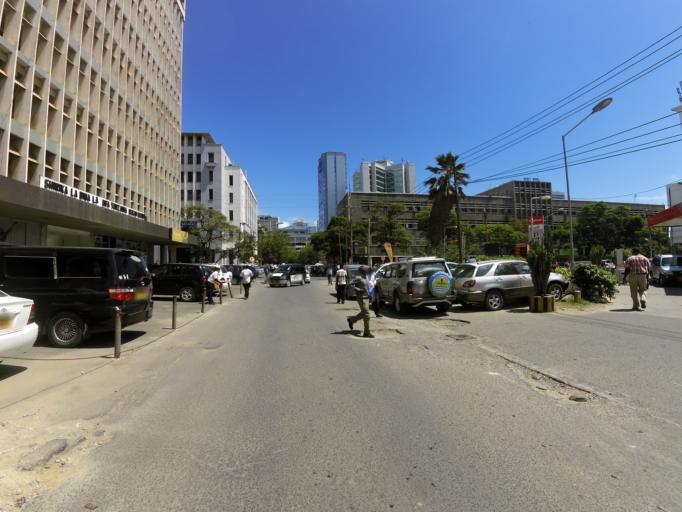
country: TZ
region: Dar es Salaam
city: Dar es Salaam
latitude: -6.8162
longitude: 39.2906
